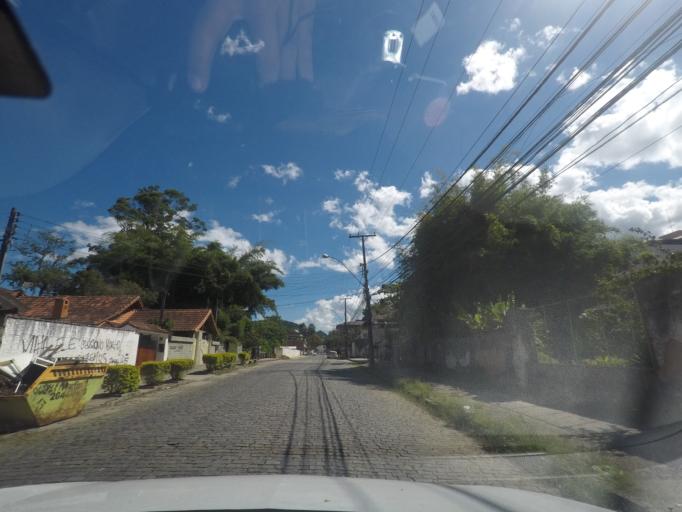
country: BR
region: Rio de Janeiro
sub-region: Teresopolis
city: Teresopolis
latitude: -22.4389
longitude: -42.9773
